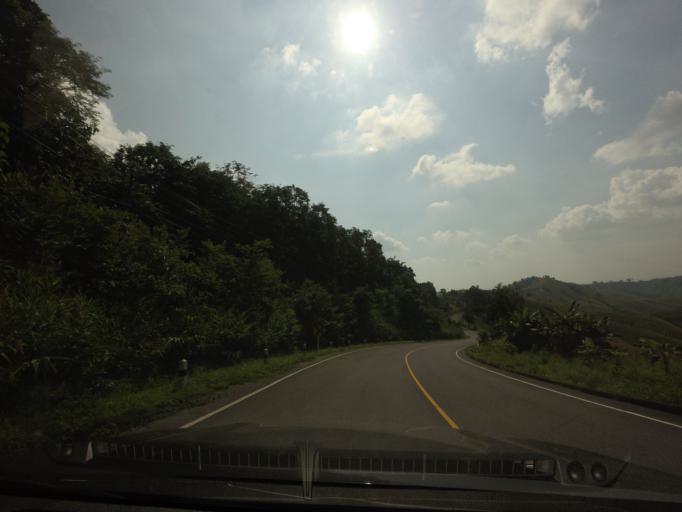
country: TH
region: Nan
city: Santi Suk
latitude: 18.9745
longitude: 100.9908
